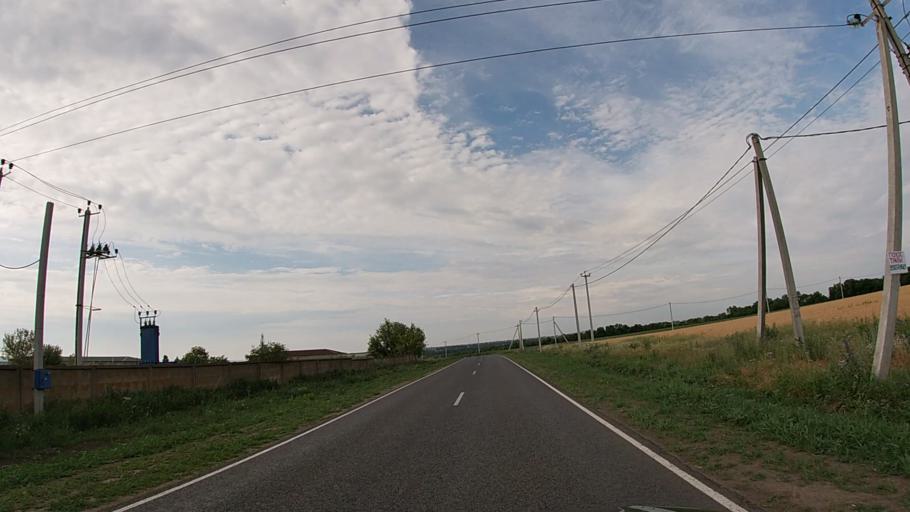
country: RU
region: Belgorod
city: Severnyy
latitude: 50.7228
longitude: 36.5845
